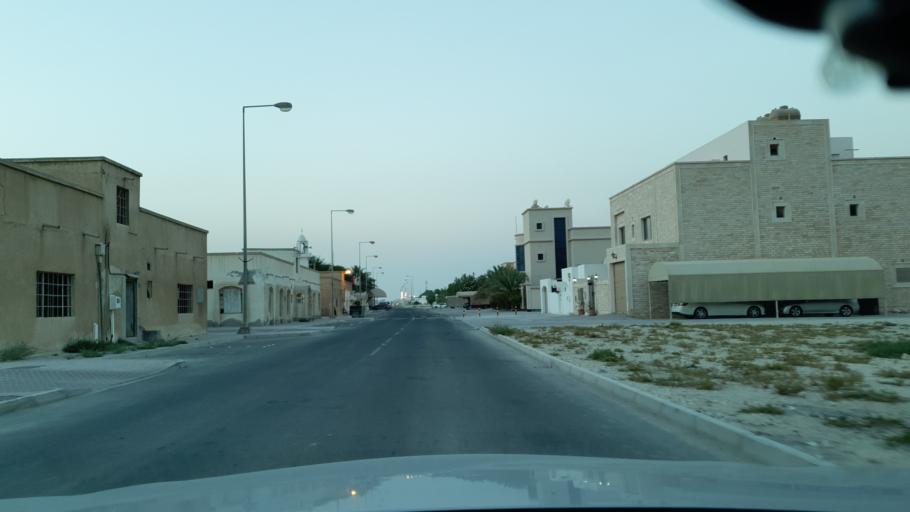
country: BH
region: Central Governorate
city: Dar Kulayb
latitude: 25.9781
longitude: 50.6152
